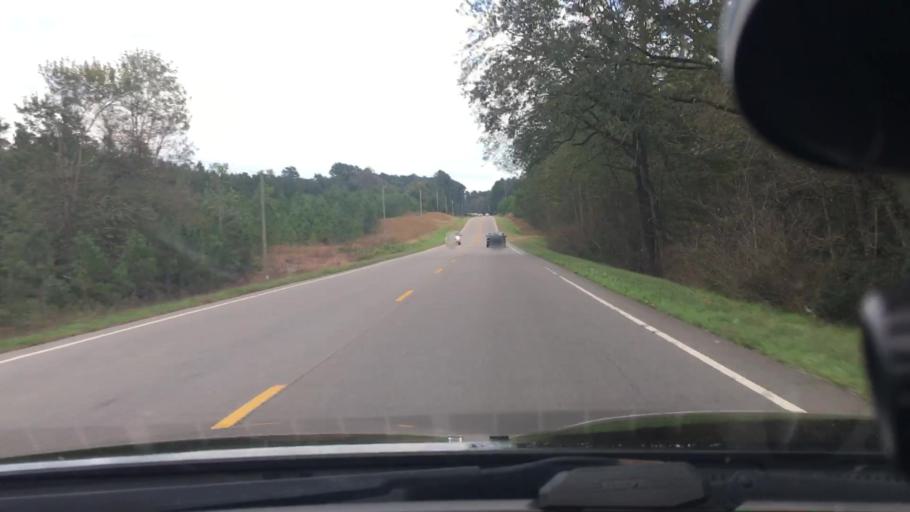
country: US
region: North Carolina
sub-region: Moore County
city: Carthage
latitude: 35.3827
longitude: -79.4846
